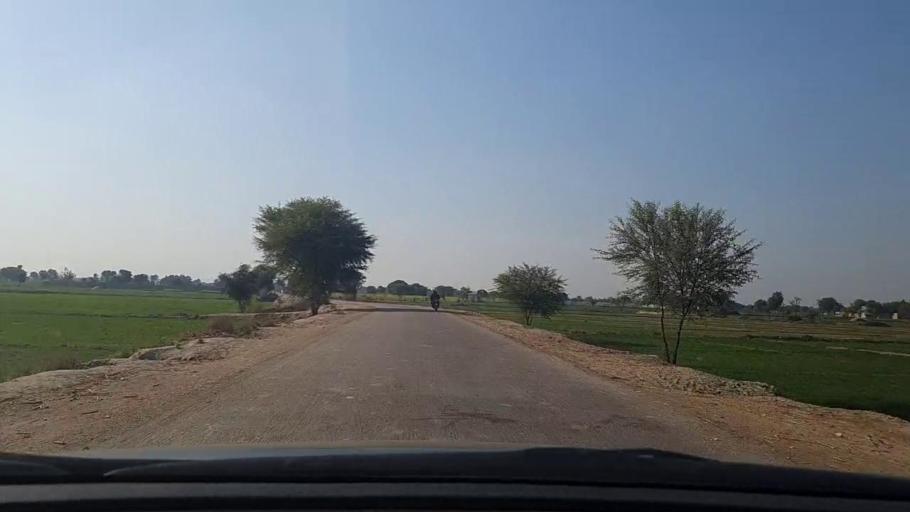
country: PK
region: Sindh
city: Daulatpur
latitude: 26.3190
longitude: 68.0519
